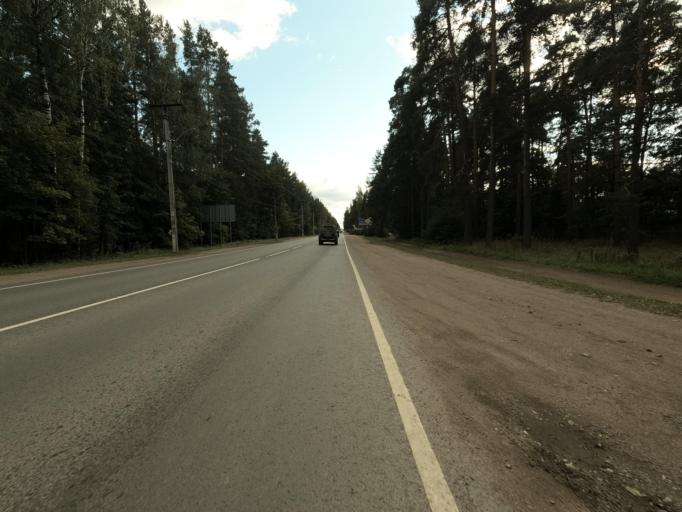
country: RU
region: Leningrad
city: Vsevolozhsk
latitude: 60.0066
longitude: 30.6643
